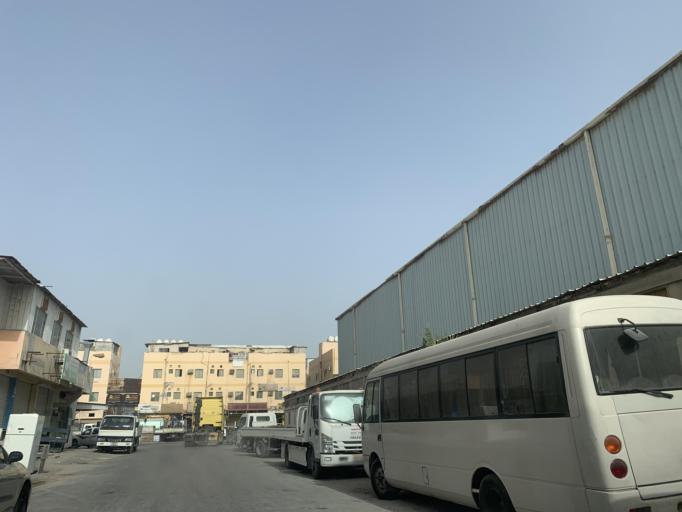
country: BH
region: Northern
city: Madinat `Isa
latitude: 26.1774
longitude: 50.5308
